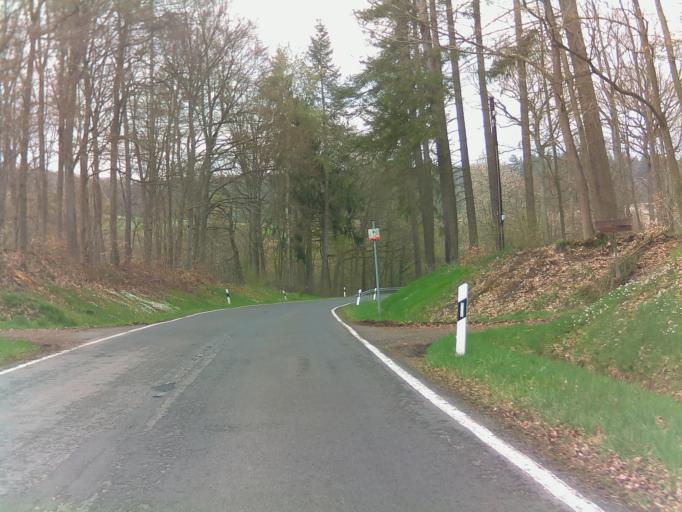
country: DE
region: Rheinland-Pfalz
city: Heinzenberg
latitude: 49.8044
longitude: 7.4755
